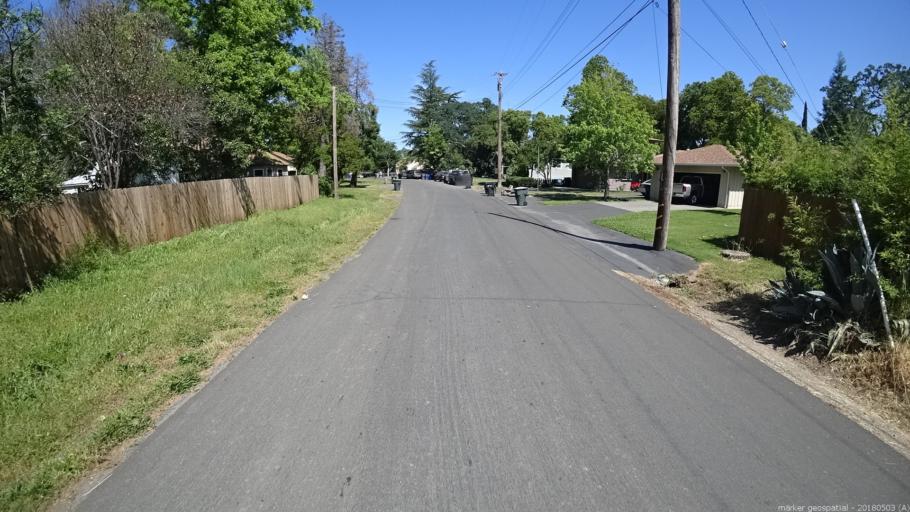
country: US
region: California
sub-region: Sacramento County
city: Arden-Arcade
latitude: 38.6293
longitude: -121.4242
